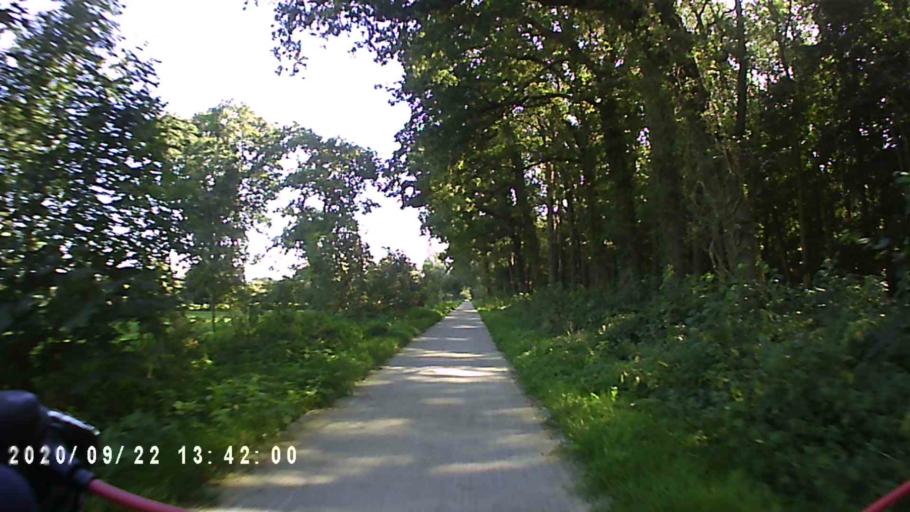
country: NL
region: Groningen
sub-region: Gemeente Leek
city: Leek
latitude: 53.1554
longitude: 6.3988
